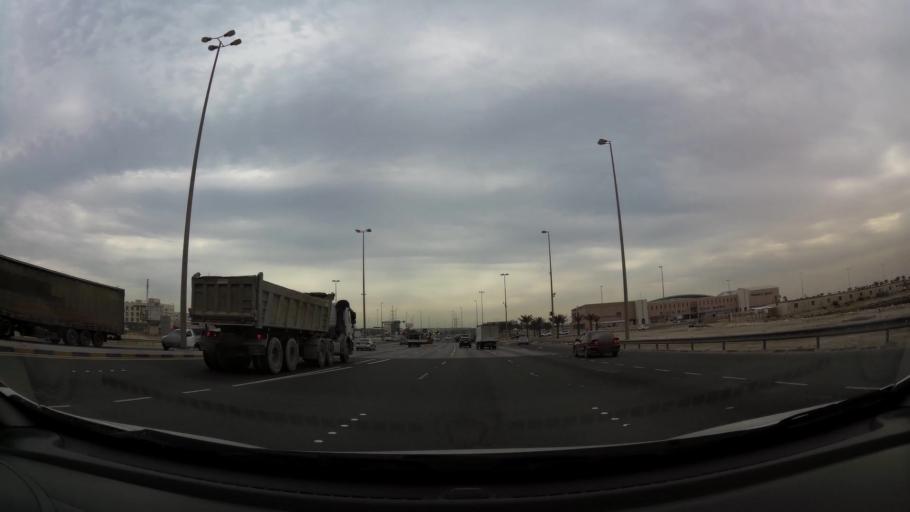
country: BH
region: Northern
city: Sitrah
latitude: 26.1729
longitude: 50.5995
